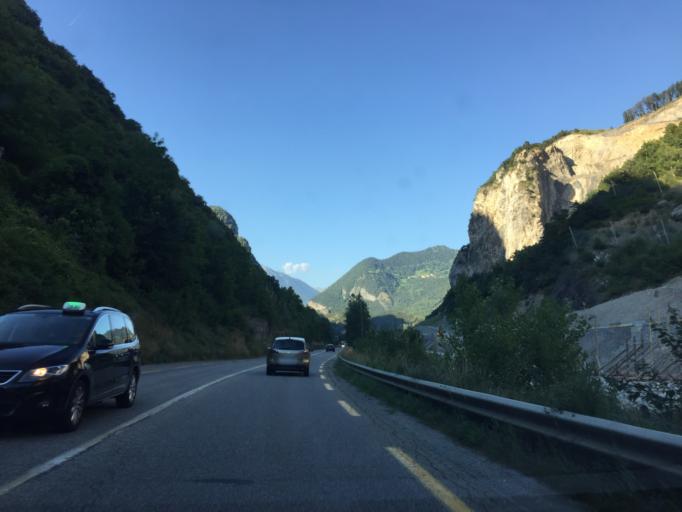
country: FR
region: Rhone-Alpes
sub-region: Departement de la Savoie
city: Moutiers
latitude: 45.4870
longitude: 6.5449
